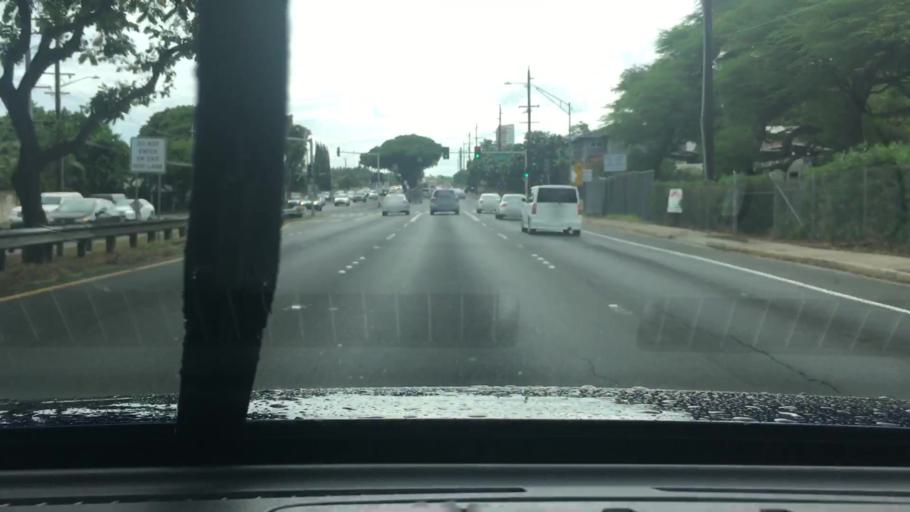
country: US
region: Hawaii
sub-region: Honolulu County
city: Waimanalo
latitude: 21.2775
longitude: -157.7755
